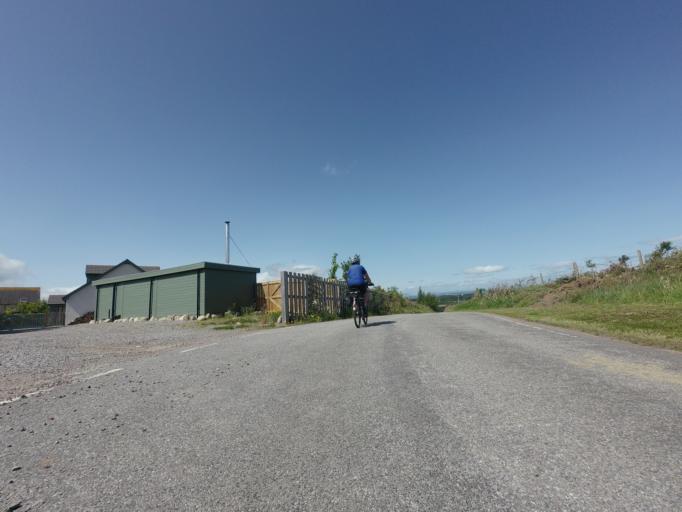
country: GB
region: Scotland
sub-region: Highland
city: Nairn
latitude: 57.5031
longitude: -3.9835
